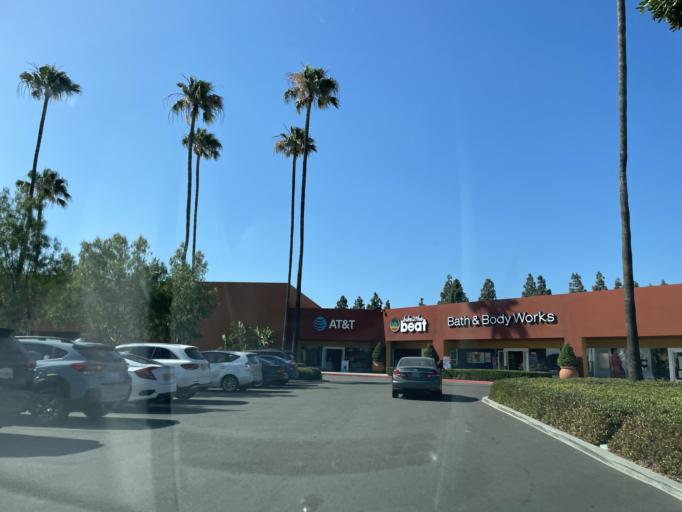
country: US
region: California
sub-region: Orange County
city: Tustin
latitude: 33.7264
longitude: -117.7936
